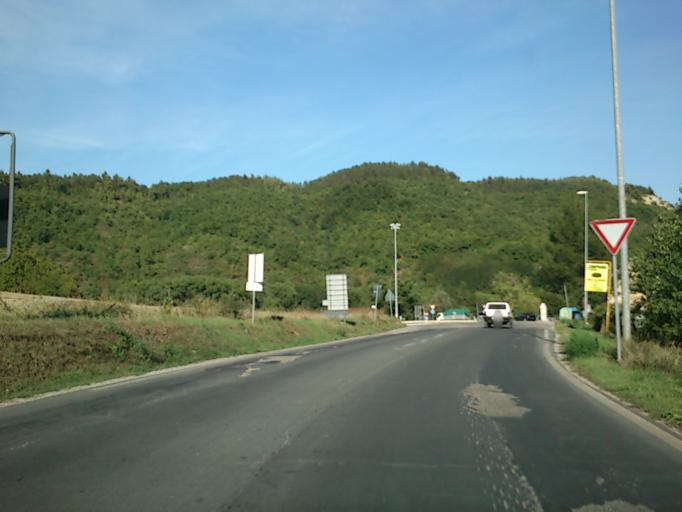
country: IT
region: The Marches
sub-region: Provincia di Pesaro e Urbino
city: Fermignano
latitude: 43.6995
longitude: 12.6618
